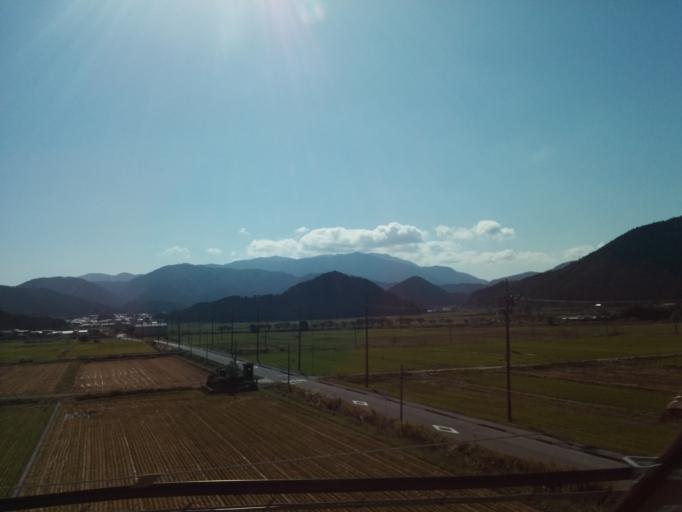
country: JP
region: Gifu
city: Tarui
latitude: 35.3619
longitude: 136.4022
